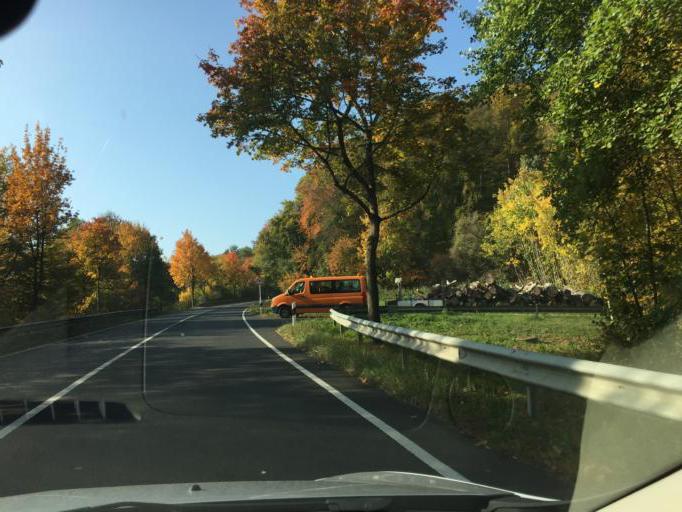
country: LU
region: Grevenmacher
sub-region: Canton de Remich
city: Bous
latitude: 49.5423
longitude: 6.3089
